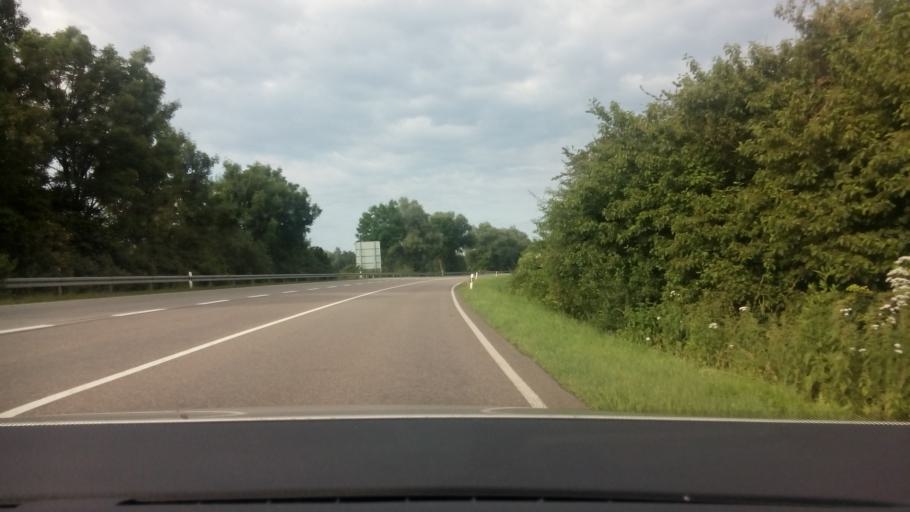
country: DE
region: Bavaria
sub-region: Upper Bavaria
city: Karlsfeld
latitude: 48.2451
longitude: 11.4746
